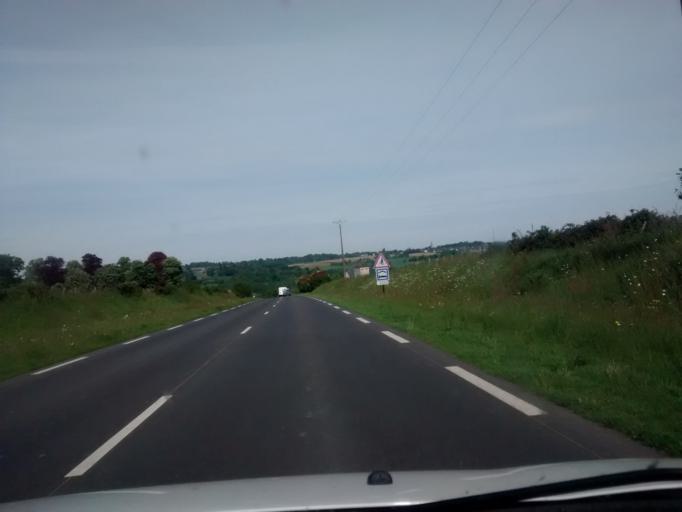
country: FR
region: Brittany
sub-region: Departement d'Ille-et-Vilaine
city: Antrain
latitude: 48.4529
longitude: -1.4821
